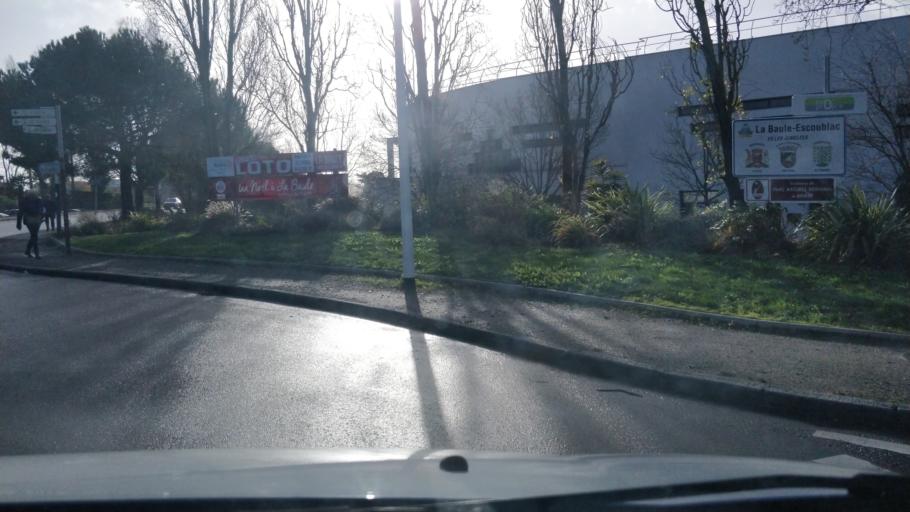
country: FR
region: Pays de la Loire
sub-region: Departement de la Loire-Atlantique
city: La Baule-Escoublac
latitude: 47.2912
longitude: -2.3955
